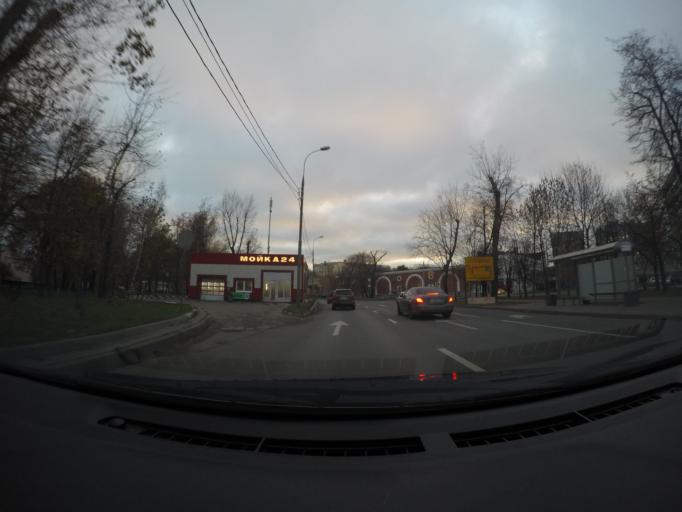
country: RU
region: Moscow
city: Taganskiy
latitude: 55.7578
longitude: 37.6698
